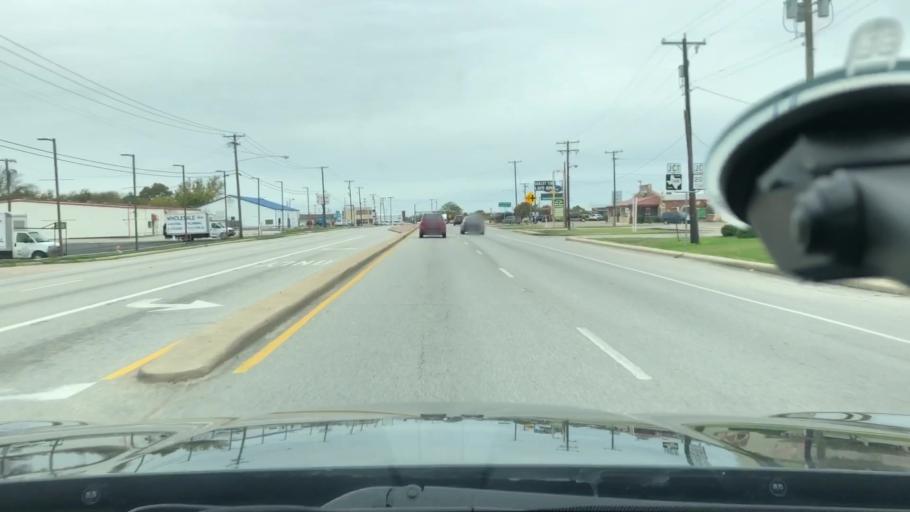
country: US
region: Texas
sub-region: Kaufman County
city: Terrell
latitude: 32.7378
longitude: -96.2988
